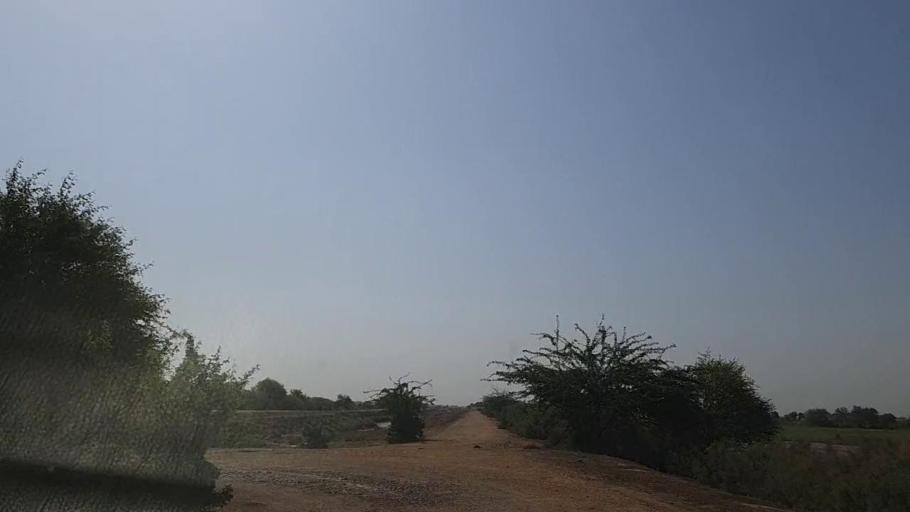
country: PK
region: Sindh
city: Daro Mehar
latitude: 24.6991
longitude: 68.1275
